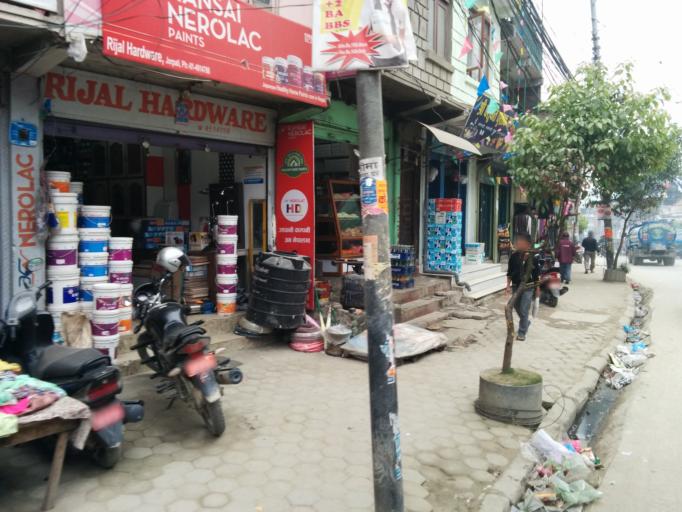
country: NP
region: Central Region
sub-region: Bagmati Zone
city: Kathmandu
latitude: 27.7216
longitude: 85.3719
